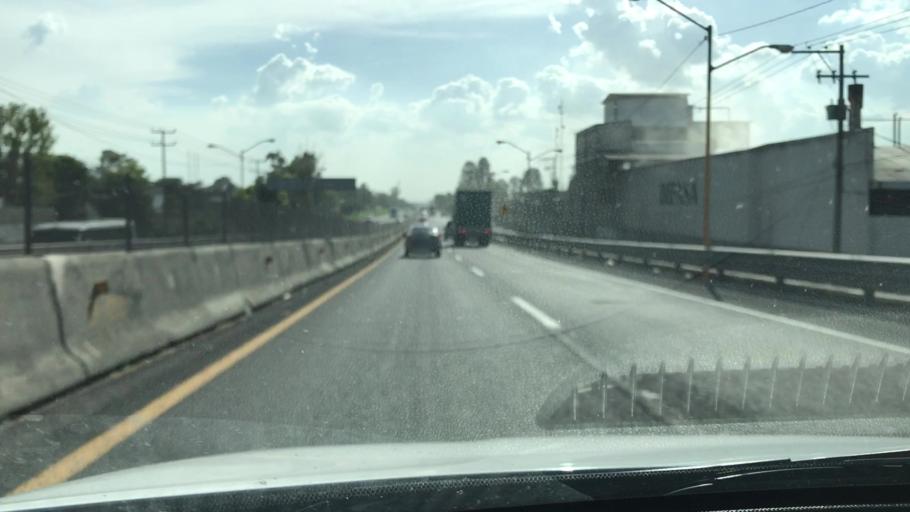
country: MX
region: Guanajuato
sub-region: Cortazar
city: Colonia la Calzada (La Olla)
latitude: 20.5109
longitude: -100.9578
